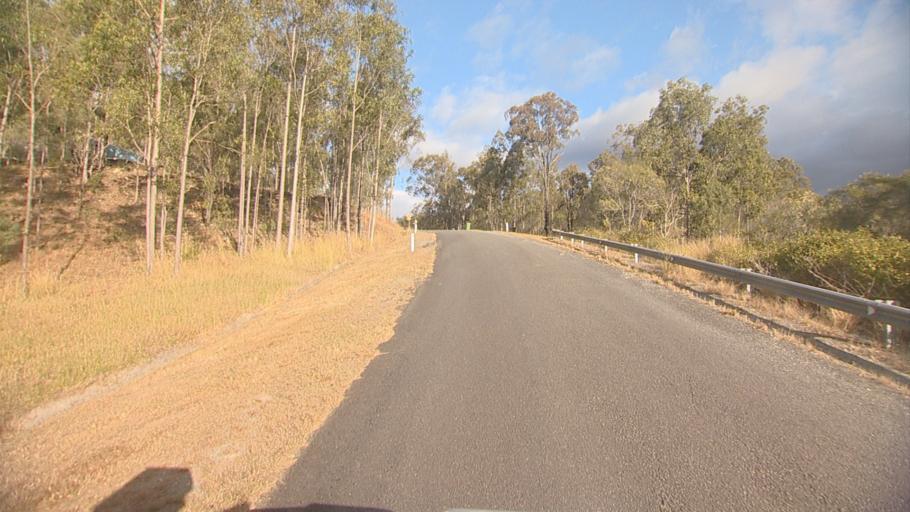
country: AU
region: Queensland
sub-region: Logan
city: Cedar Vale
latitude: -27.9068
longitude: 153.0638
